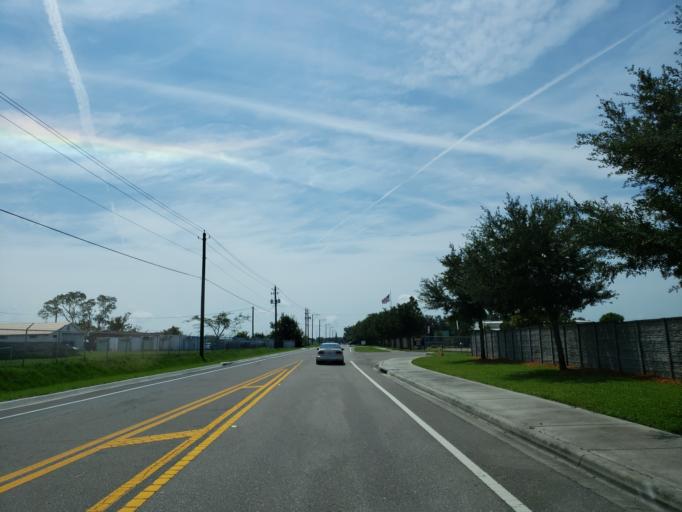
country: US
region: Florida
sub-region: Hillsborough County
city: Riverview
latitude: 27.8439
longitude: -82.3433
